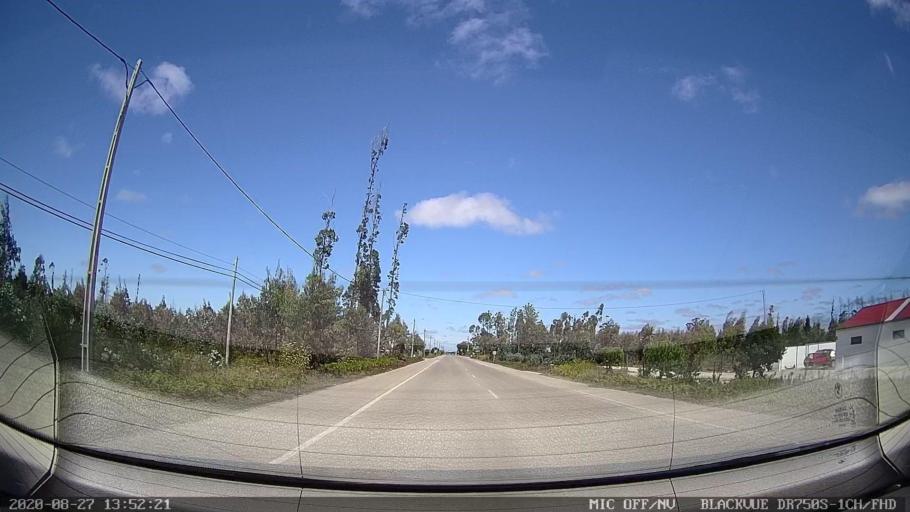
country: PT
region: Coimbra
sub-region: Mira
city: Mira
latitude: 40.3400
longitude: -8.7499
